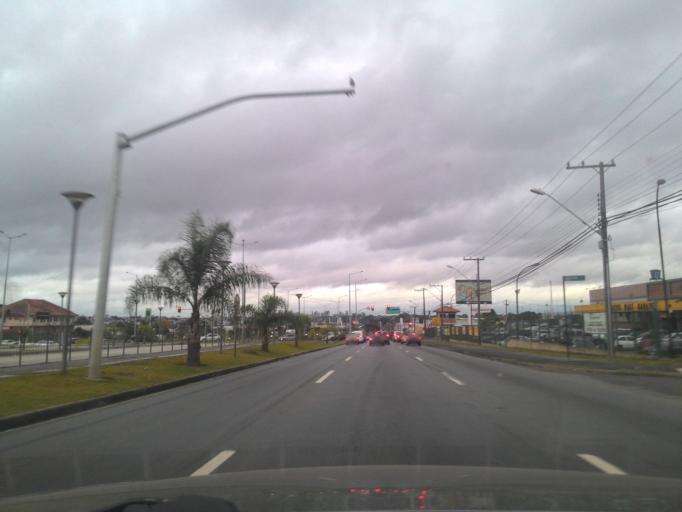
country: BR
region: Parana
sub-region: Curitiba
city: Curitiba
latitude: -25.4854
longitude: -49.2666
